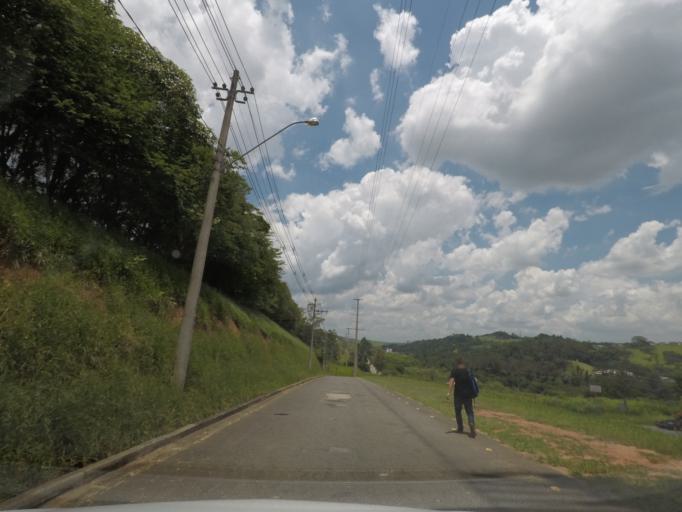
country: BR
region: Sao Paulo
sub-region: Vinhedo
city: Vinhedo
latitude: -23.0608
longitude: -47.0043
